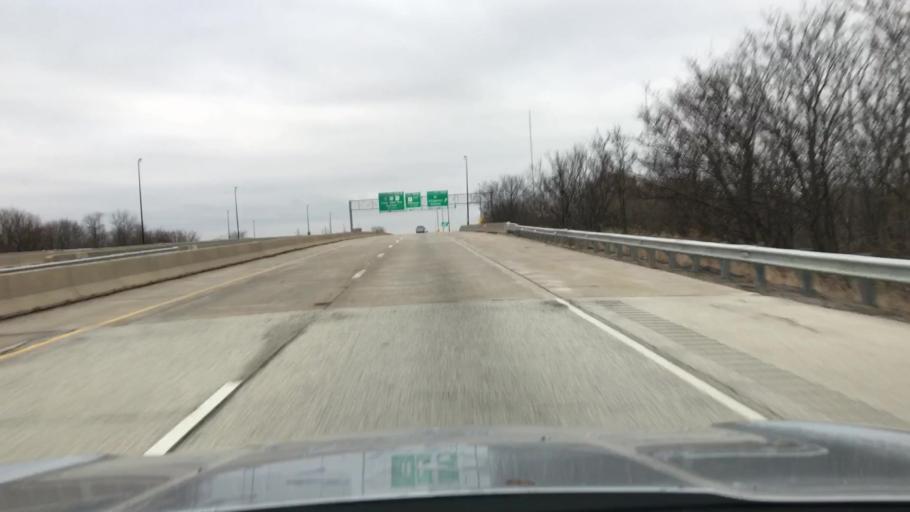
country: US
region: Illinois
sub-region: Sangamon County
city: Grandview
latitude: 39.8364
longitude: -89.5937
